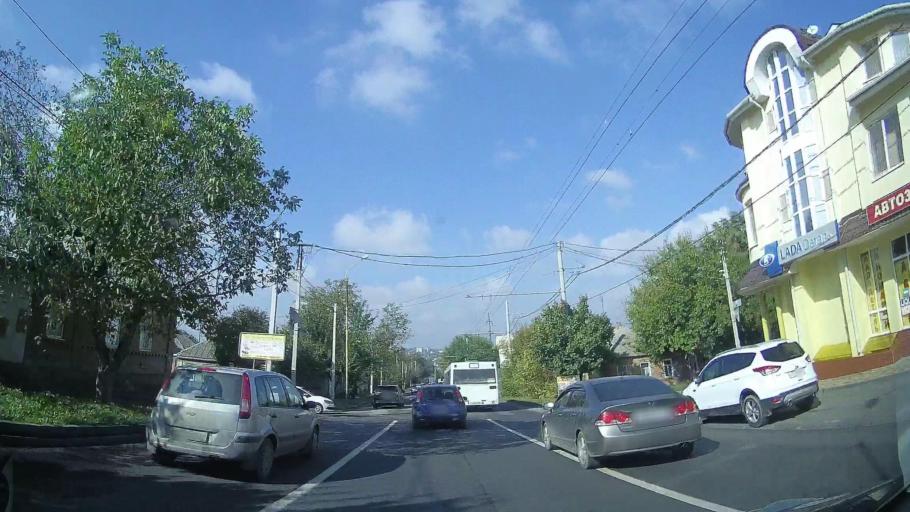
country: RU
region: Rostov
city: Severnyy
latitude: 47.2580
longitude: 39.6939
